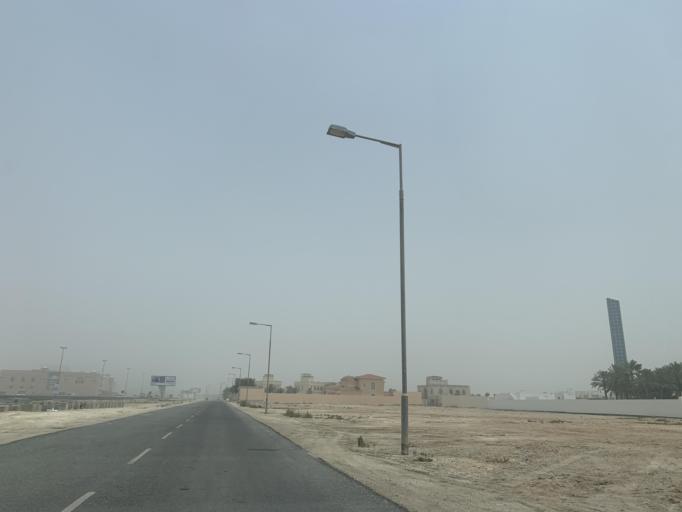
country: BH
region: Central Governorate
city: Madinat Hamad
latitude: 26.1725
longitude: 50.4714
